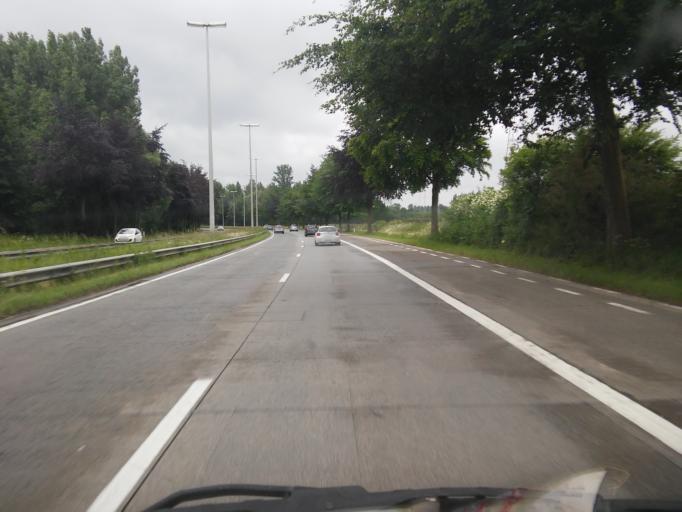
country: BE
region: Flanders
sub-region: Provincie Oost-Vlaanderen
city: Ninove
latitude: 50.8624
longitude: 4.0249
